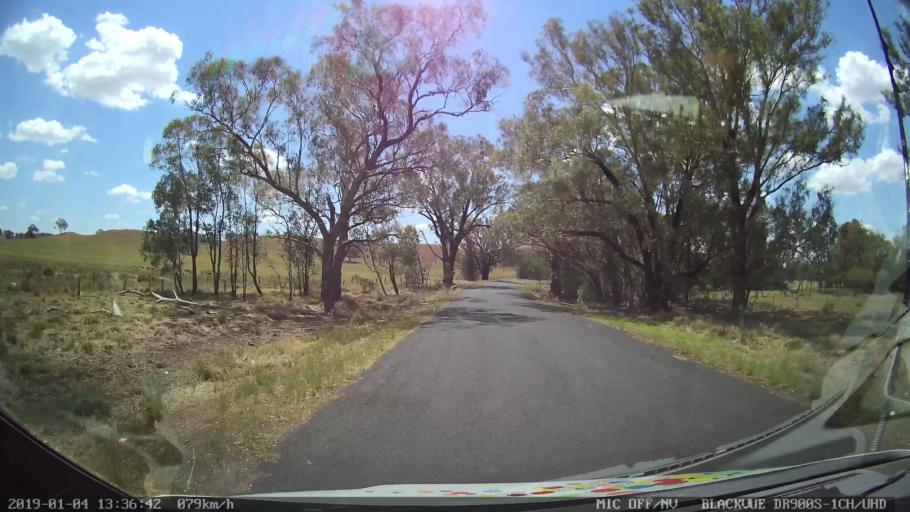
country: AU
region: New South Wales
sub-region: Dubbo Municipality
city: Dubbo
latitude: -32.5576
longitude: 148.5378
